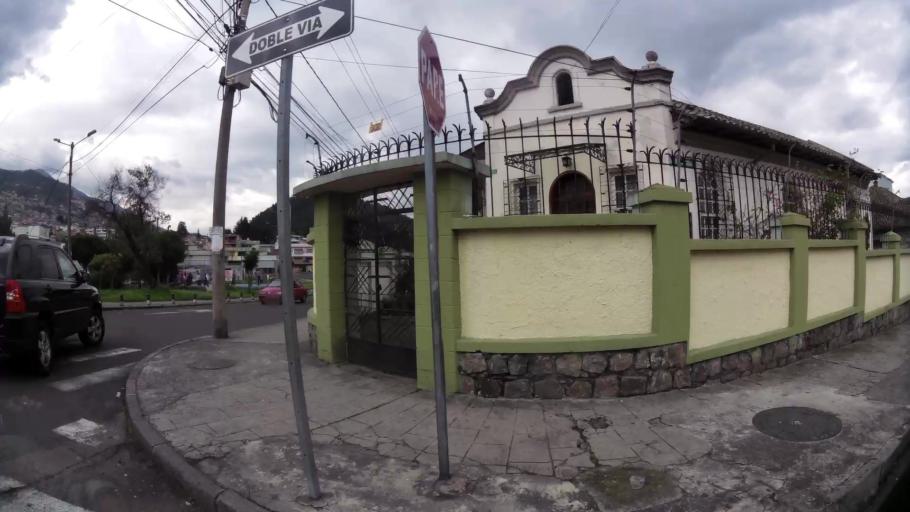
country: EC
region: Pichincha
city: Quito
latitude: -0.2416
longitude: -78.5256
